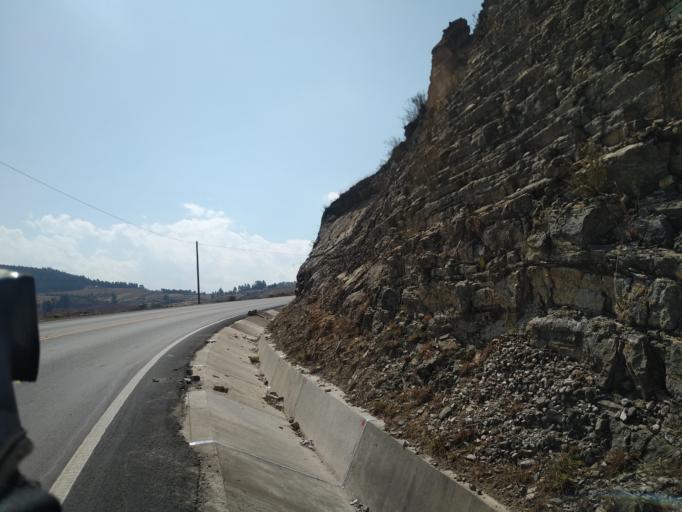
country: PE
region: Cajamarca
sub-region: Provincia de Cajamarca
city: Llacanora
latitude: -7.2057
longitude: -78.3918
